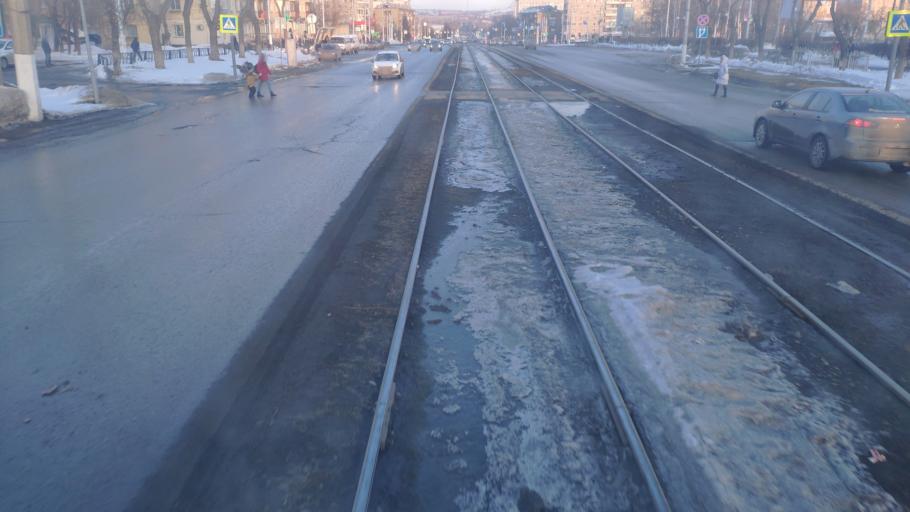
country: RU
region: Chelyabinsk
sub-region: Gorod Magnitogorsk
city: Magnitogorsk
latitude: 53.3980
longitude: 58.9740
